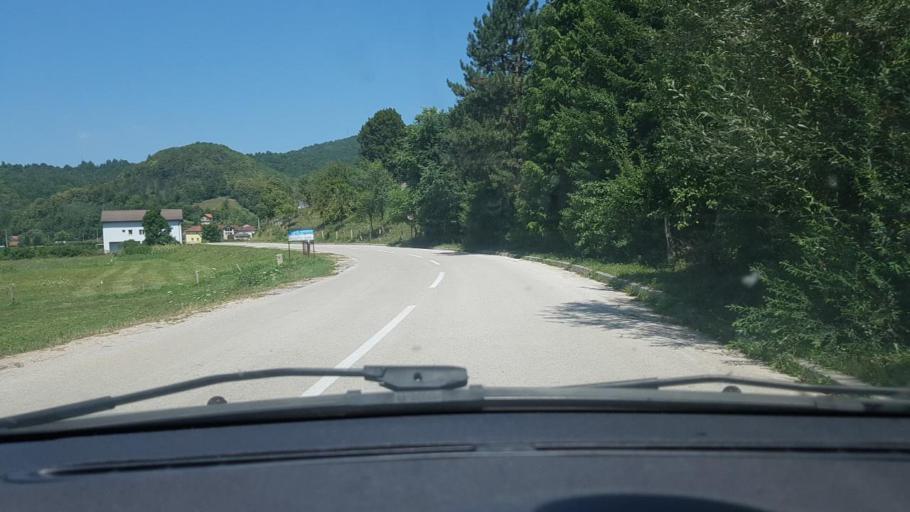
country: BA
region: Federation of Bosnia and Herzegovina
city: Orasac
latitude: 44.5629
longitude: 16.1015
